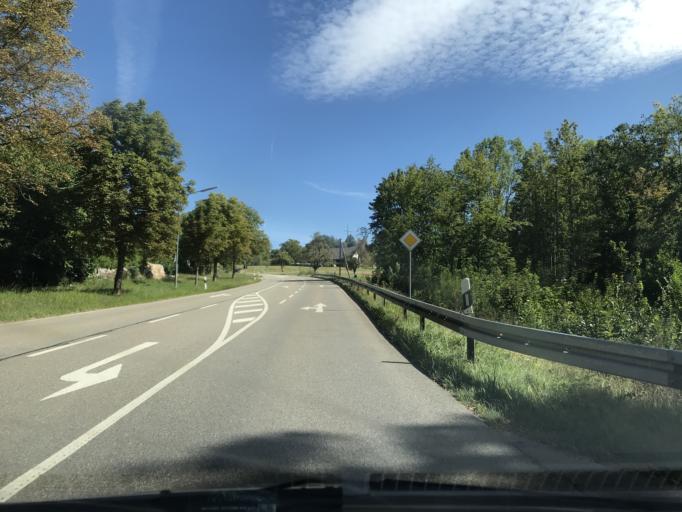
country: DE
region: Baden-Wuerttemberg
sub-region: Freiburg Region
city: Schopfheim
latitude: 47.6439
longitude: 7.8305
